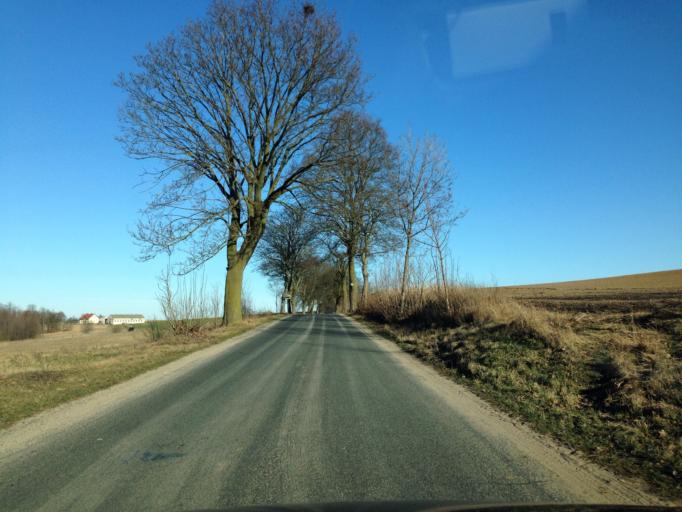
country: PL
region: Kujawsko-Pomorskie
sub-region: Powiat brodnicki
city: Brzozie
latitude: 53.3556
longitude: 19.6381
